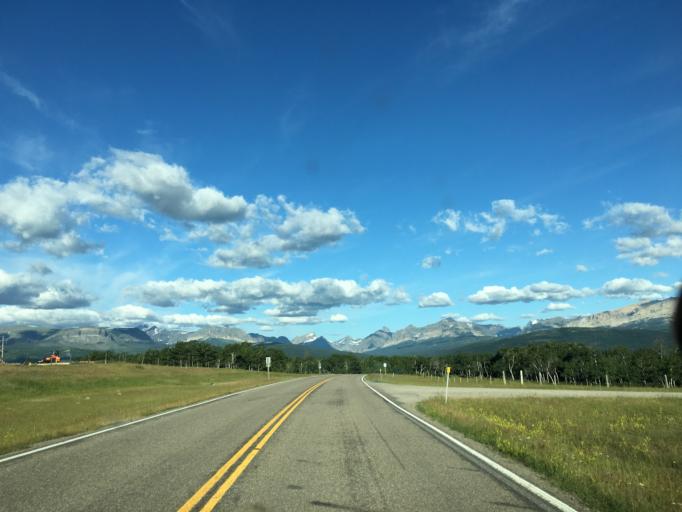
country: CA
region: Alberta
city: Cardston
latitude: 48.8461
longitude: -113.3642
